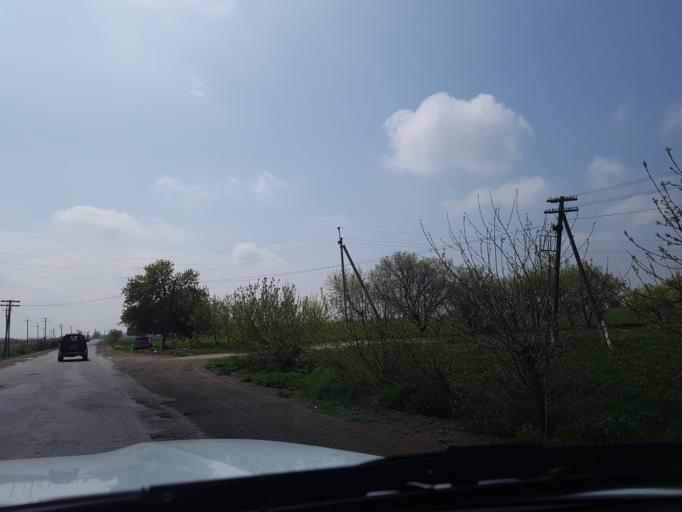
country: TM
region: Lebap
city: Turkmenabat
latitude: 38.9574
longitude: 63.6758
